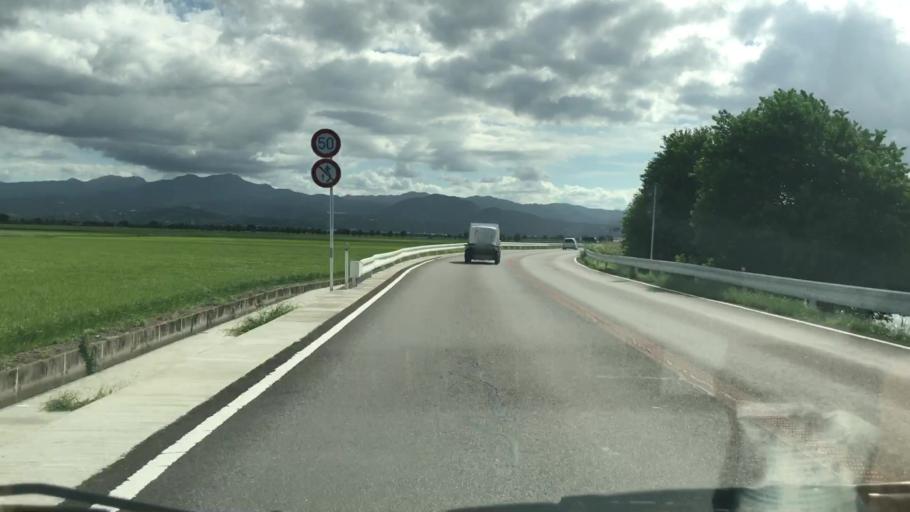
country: JP
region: Saga Prefecture
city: Kashima
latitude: 33.1391
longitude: 130.1430
